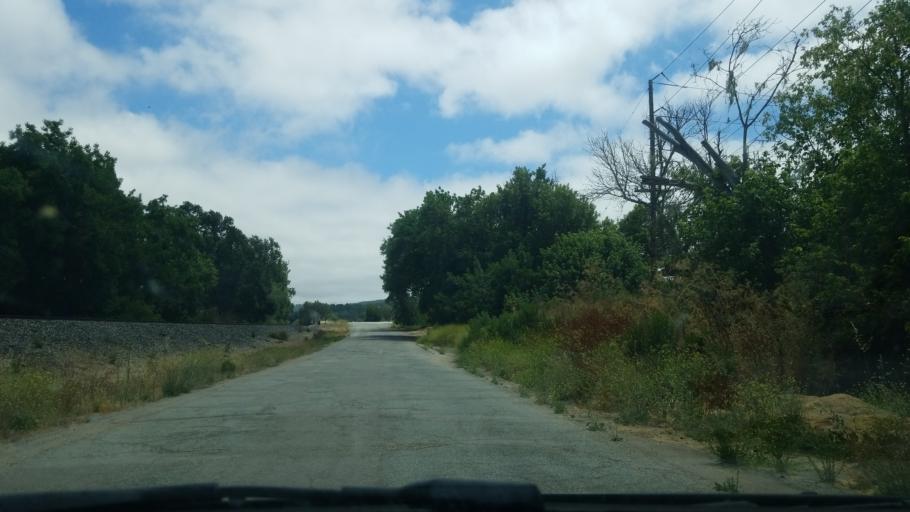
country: US
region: California
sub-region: San Luis Obispo County
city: Templeton
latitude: 35.5391
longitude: -120.7108
